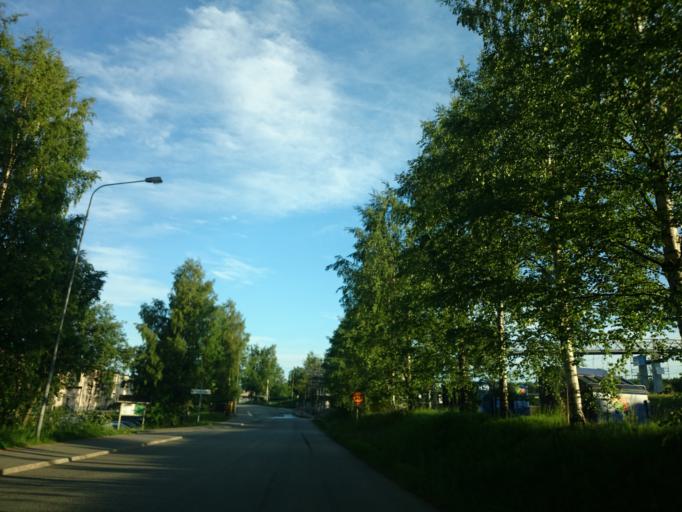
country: SE
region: Vaesternorrland
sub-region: Sundsvalls Kommun
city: Stockvik
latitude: 62.3516
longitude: 17.3658
